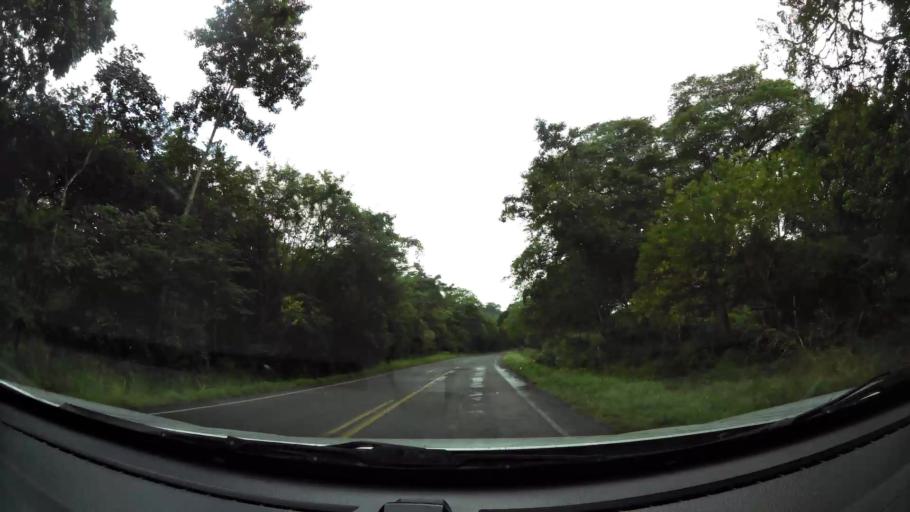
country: CR
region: Guanacaste
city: Juntas
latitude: 10.2356
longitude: -84.9843
